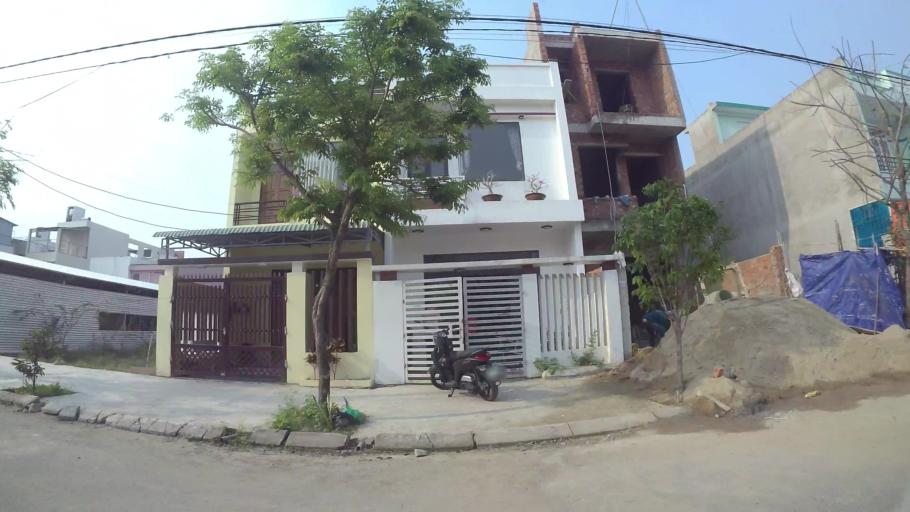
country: VN
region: Da Nang
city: Cam Le
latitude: 16.0074
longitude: 108.2257
